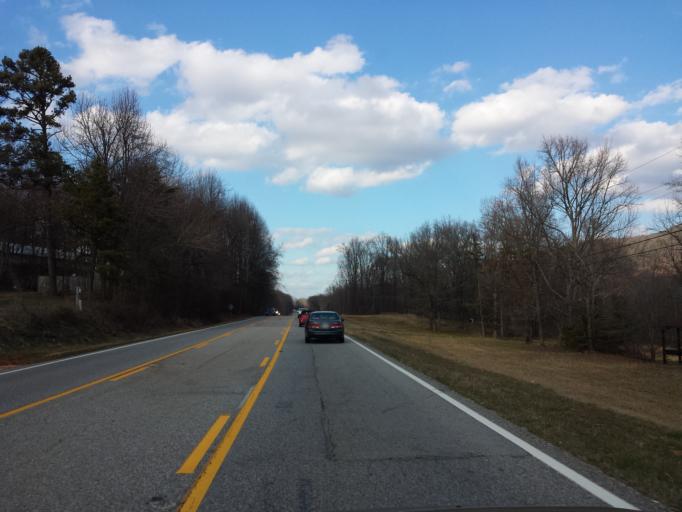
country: US
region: Georgia
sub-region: White County
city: Cleveland
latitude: 34.5553
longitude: -83.7907
